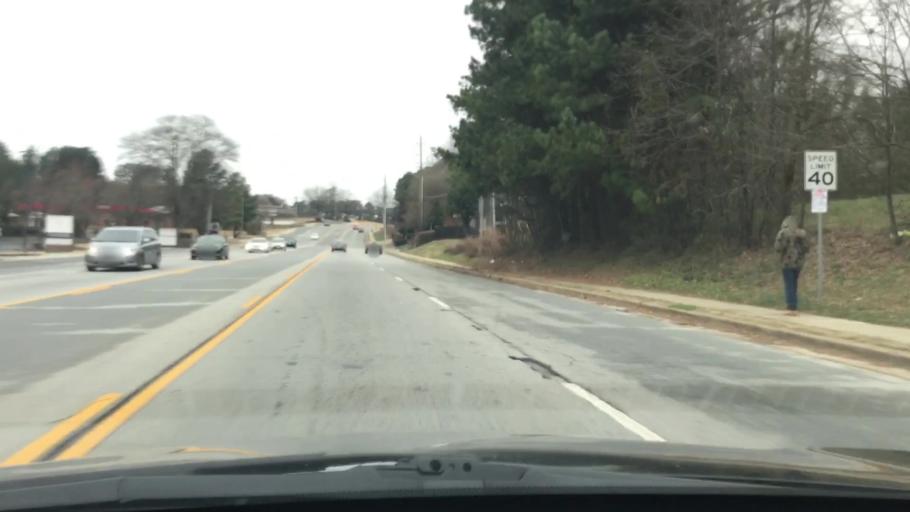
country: US
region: Georgia
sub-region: Gwinnett County
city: Lilburn
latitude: 33.9420
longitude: -84.1173
